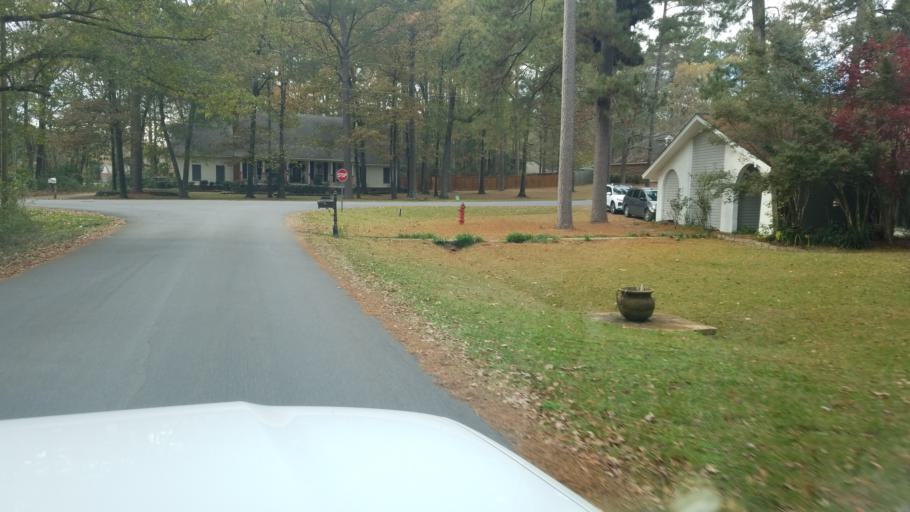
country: US
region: Mississippi
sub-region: Madison County
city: Ridgeland
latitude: 32.3835
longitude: -90.0324
